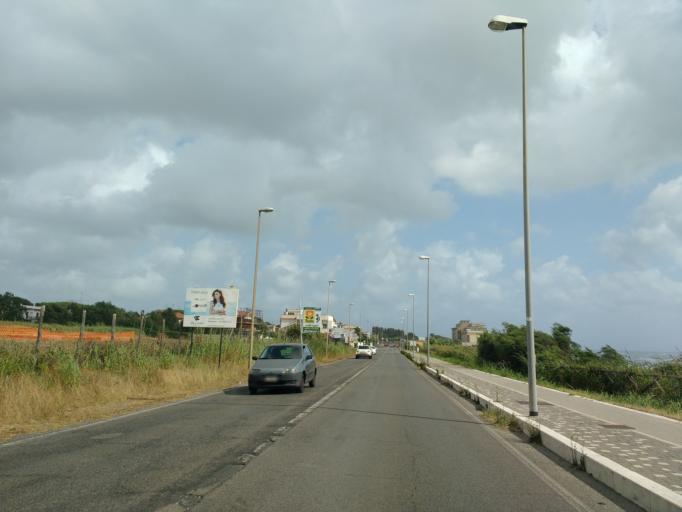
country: IT
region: Latium
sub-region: Citta metropolitana di Roma Capitale
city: Anzio
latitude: 41.4716
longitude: 12.6061
